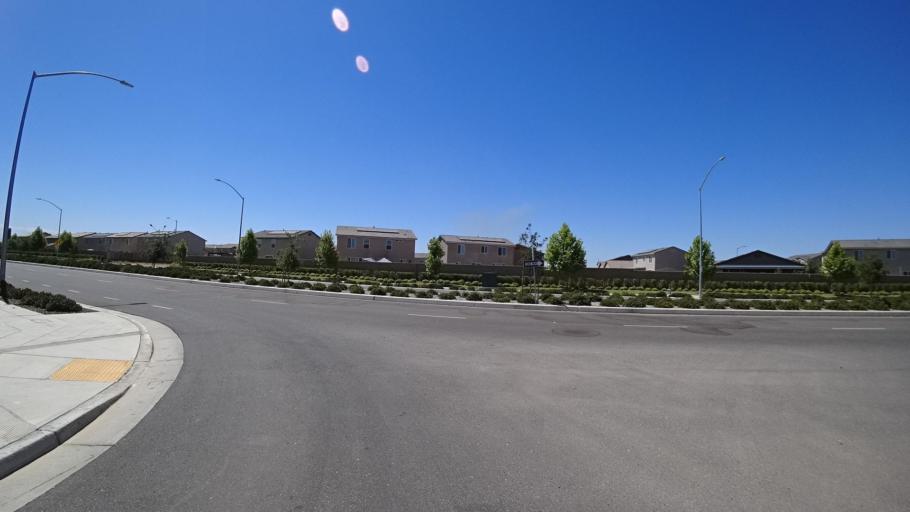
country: US
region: California
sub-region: Fresno County
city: Sunnyside
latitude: 36.7209
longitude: -119.6667
